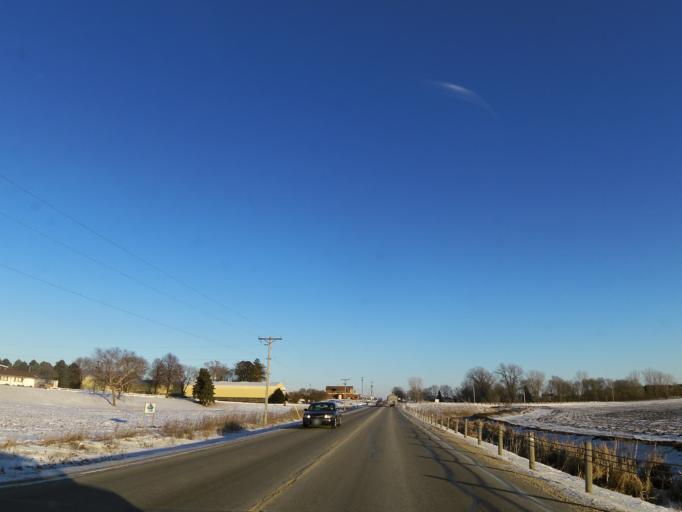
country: US
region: Minnesota
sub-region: Rice County
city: Northfield
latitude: 44.5437
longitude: -93.1397
